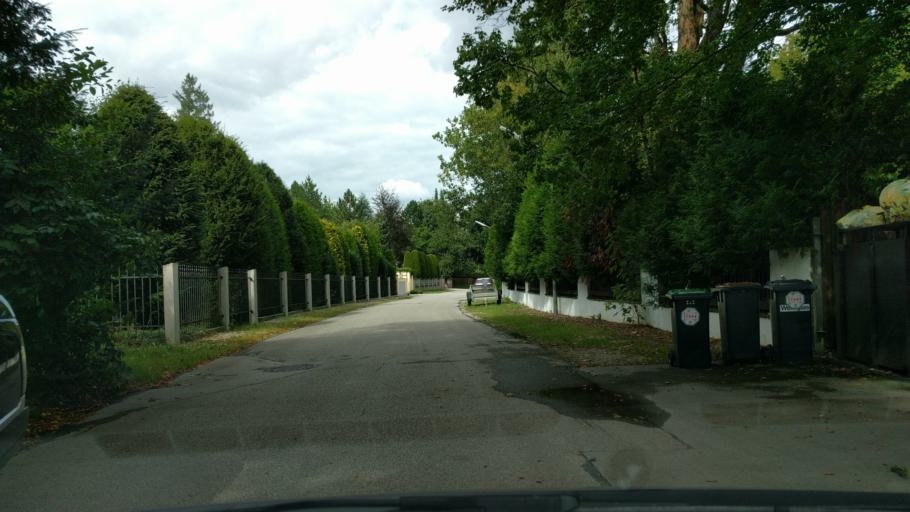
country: DE
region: Bavaria
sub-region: Upper Bavaria
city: Pullach im Isartal
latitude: 48.0606
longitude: 11.5492
